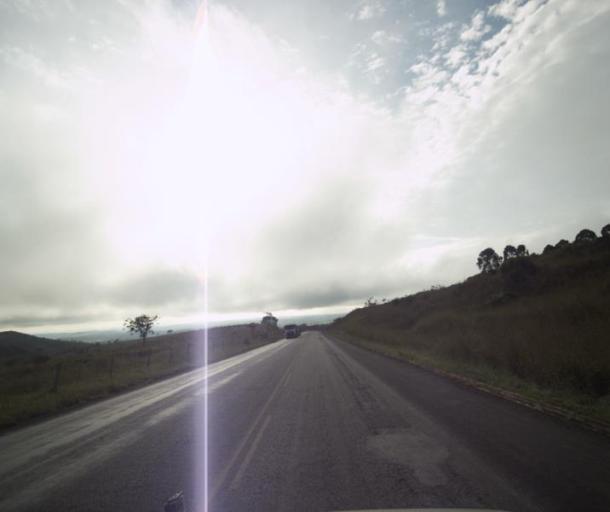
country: BR
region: Goias
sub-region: Pirenopolis
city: Pirenopolis
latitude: -15.7527
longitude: -48.7460
